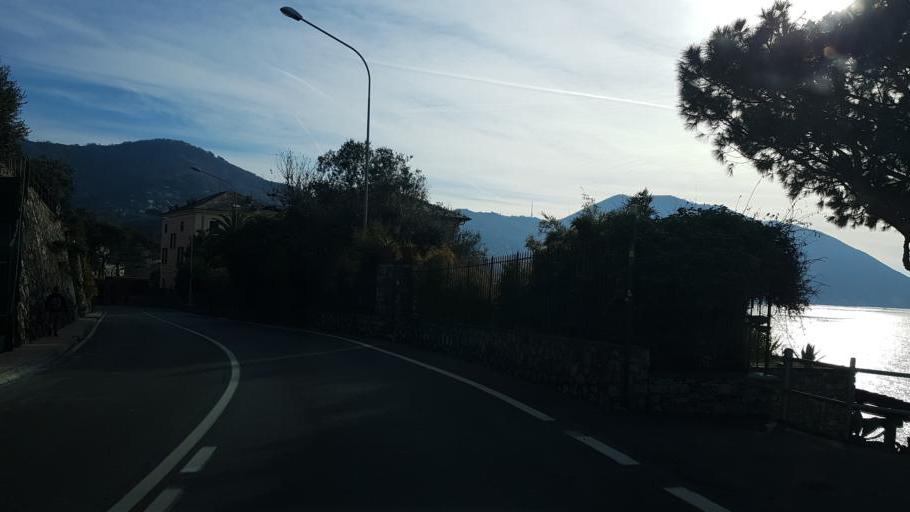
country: IT
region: Liguria
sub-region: Provincia di Genova
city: Recco
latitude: 44.3611
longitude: 9.1365
